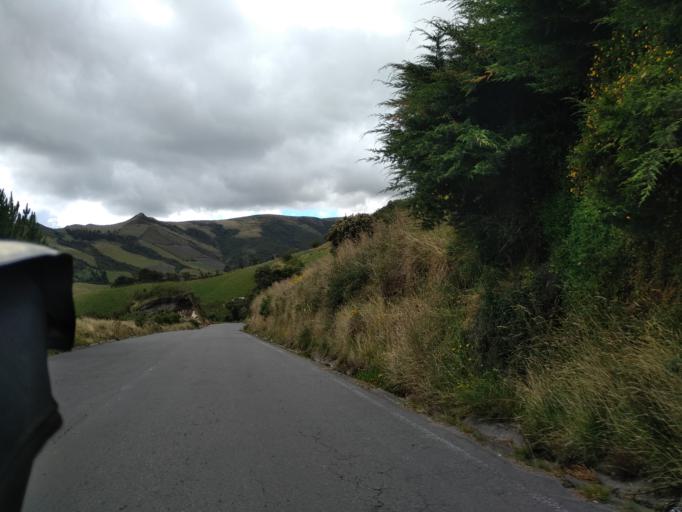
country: EC
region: Cotopaxi
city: Saquisili
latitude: -0.7294
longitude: -78.7534
